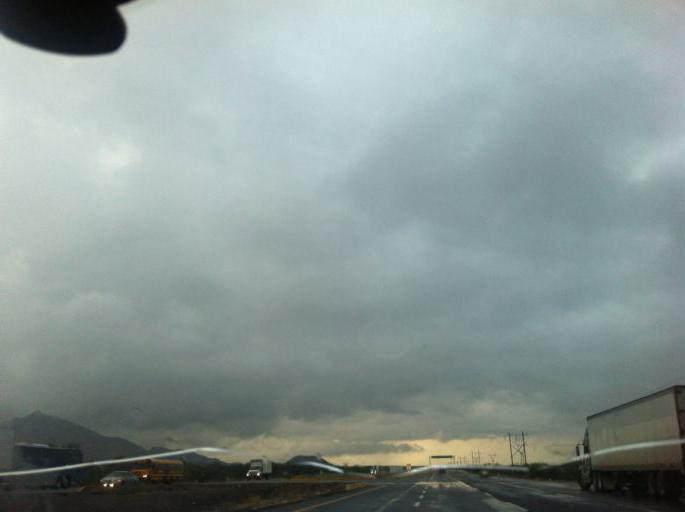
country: MX
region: Sonora
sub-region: Hermosillo
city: Estacion Zamora
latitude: 29.2218
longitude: -110.9304
